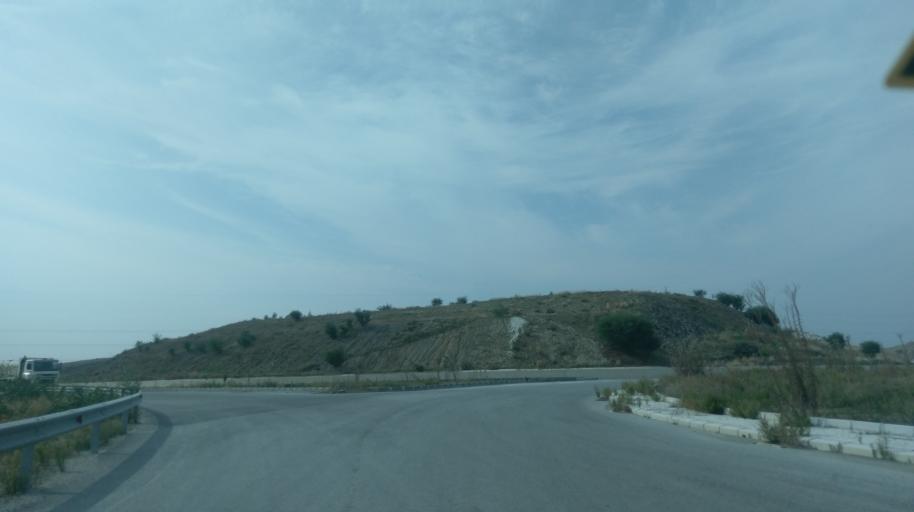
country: CY
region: Lefkosia
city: Nicosia
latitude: 35.2297
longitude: 33.4006
